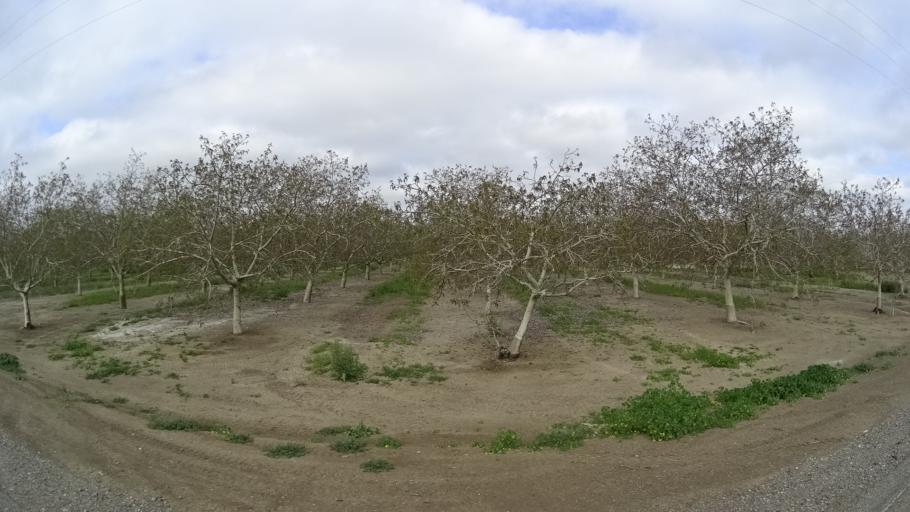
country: US
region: California
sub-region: Glenn County
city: Willows
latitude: 39.4494
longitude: -121.9679
